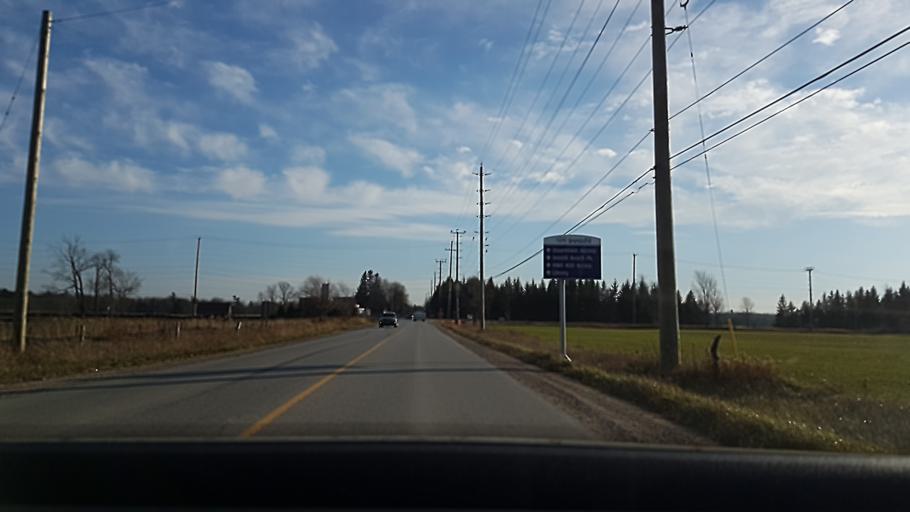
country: CA
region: Ontario
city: Barrie
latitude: 44.3798
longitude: -79.5541
